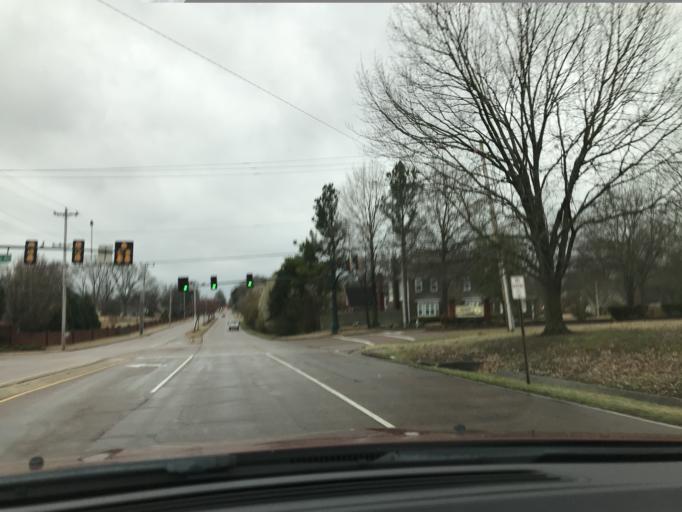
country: US
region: Tennessee
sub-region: Shelby County
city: Collierville
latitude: 35.0619
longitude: -89.6860
